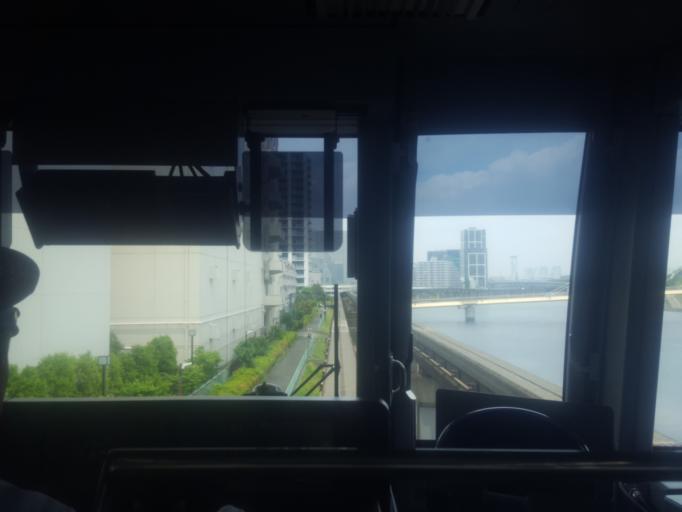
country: JP
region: Kanagawa
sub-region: Kawasaki-shi
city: Kawasaki
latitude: 35.5981
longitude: 139.7472
